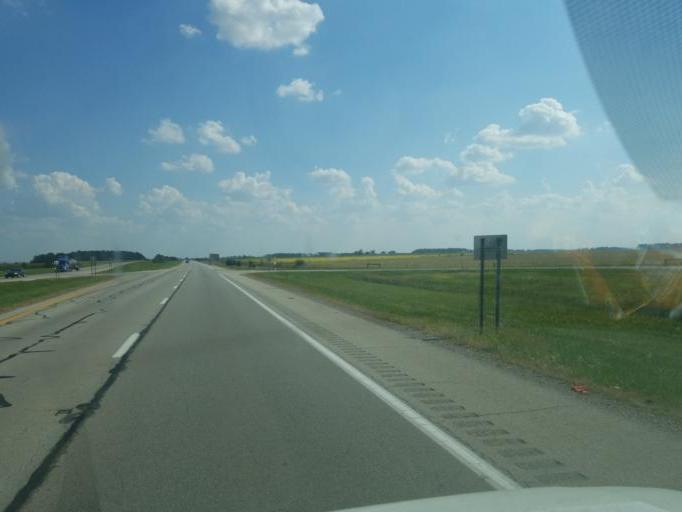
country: US
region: Ohio
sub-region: Van Wert County
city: Convoy
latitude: 40.9753
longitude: -84.7617
